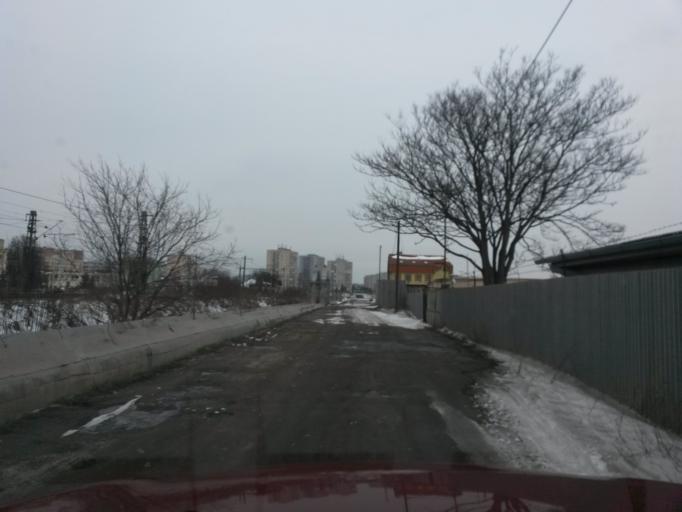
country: SK
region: Kosicky
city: Kosice
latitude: 48.7065
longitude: 21.2672
